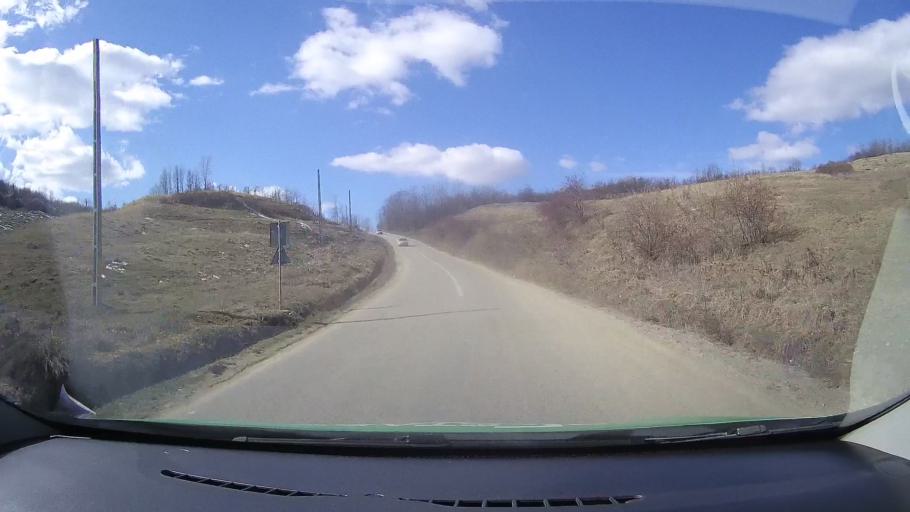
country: RO
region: Dambovita
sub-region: Comuna Glodeni
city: Laculete
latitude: 45.0248
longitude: 25.4280
